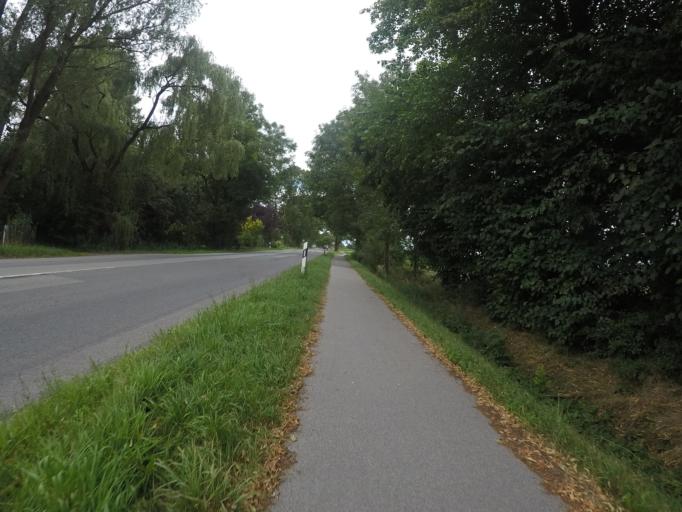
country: DE
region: Lower Saxony
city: Himmelpforten
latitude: 53.6400
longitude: 9.2967
